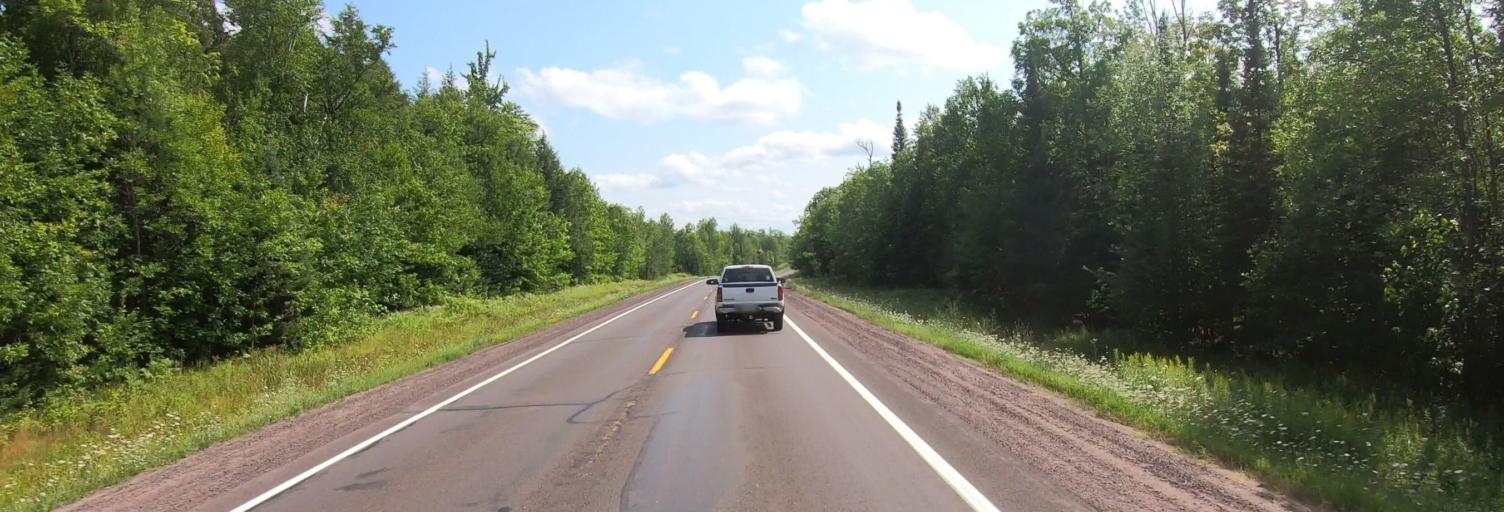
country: US
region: Michigan
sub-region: Ontonagon County
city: Ontonagon
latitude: 46.8175
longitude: -88.9961
